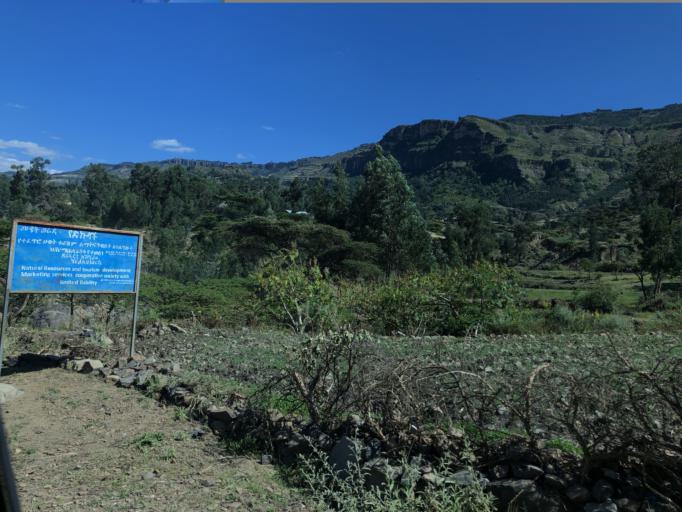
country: ET
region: Amhara
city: Lalibela
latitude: 11.7261
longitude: 38.9311
